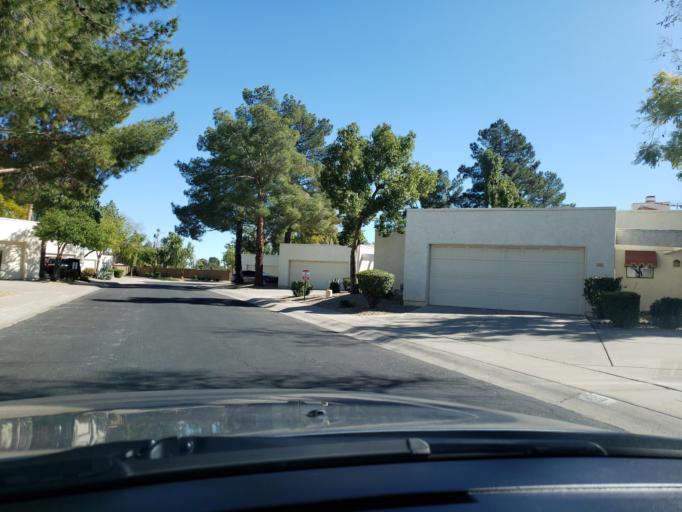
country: US
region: Arizona
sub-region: Maricopa County
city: Paradise Valley
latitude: 33.6133
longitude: -111.9908
